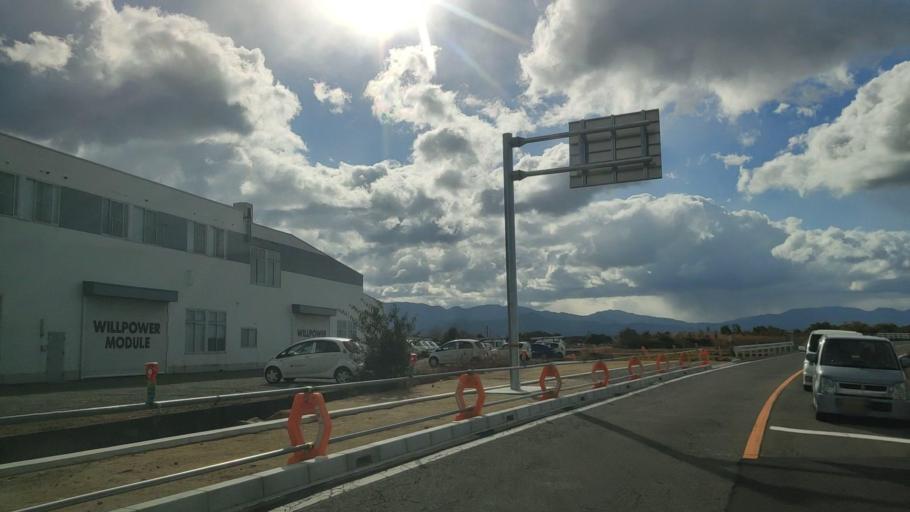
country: JP
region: Ehime
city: Masaki-cho
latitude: 33.8202
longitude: 132.7133
